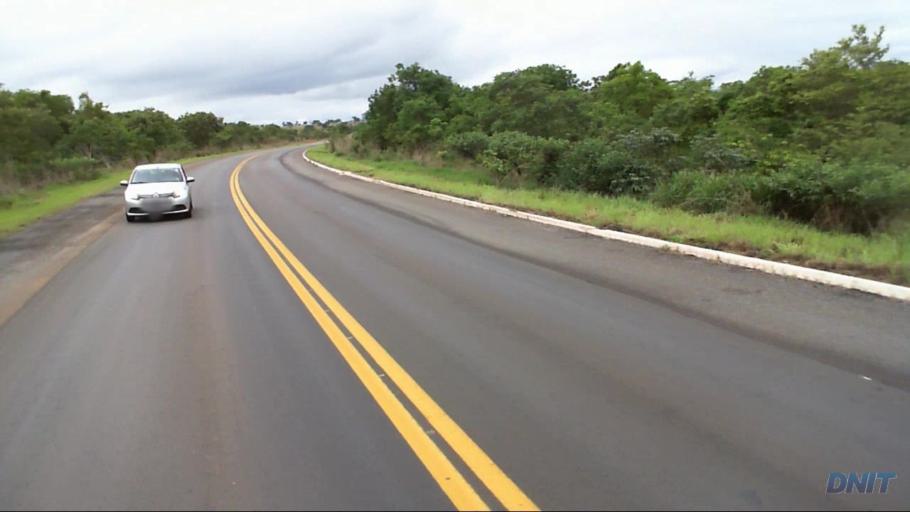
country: BR
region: Goias
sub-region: Padre Bernardo
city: Padre Bernardo
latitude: -15.2206
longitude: -48.5487
